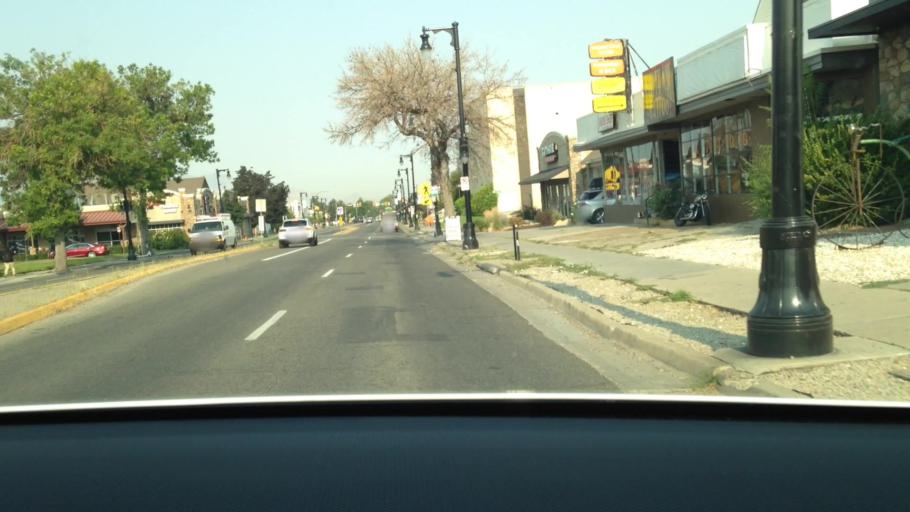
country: US
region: Utah
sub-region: Salt Lake County
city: South Salt Lake
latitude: 40.7255
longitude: -111.8673
